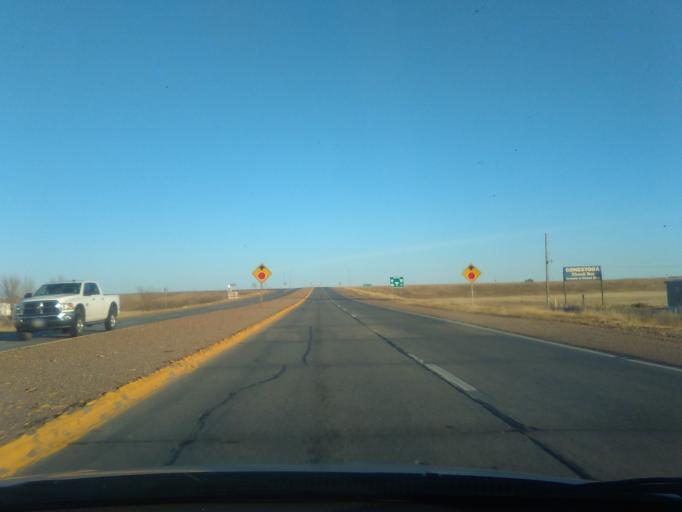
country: US
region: Nebraska
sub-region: Cheyenne County
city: Sidney
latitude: 41.1446
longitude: -102.9504
